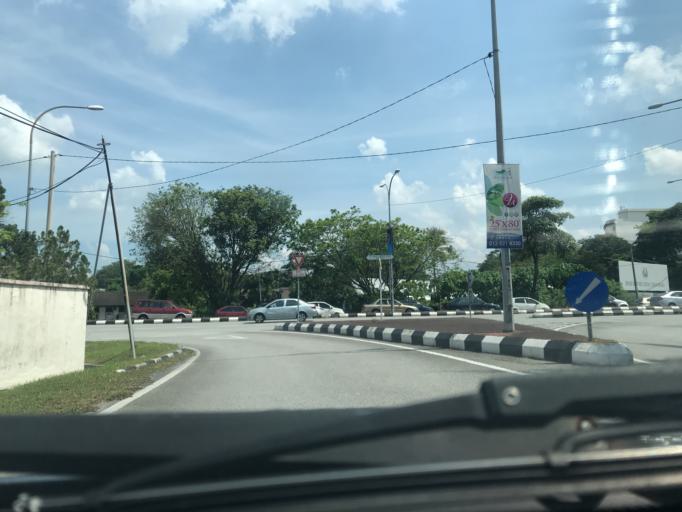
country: MY
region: Perak
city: Ipoh
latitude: 4.6022
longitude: 101.0978
